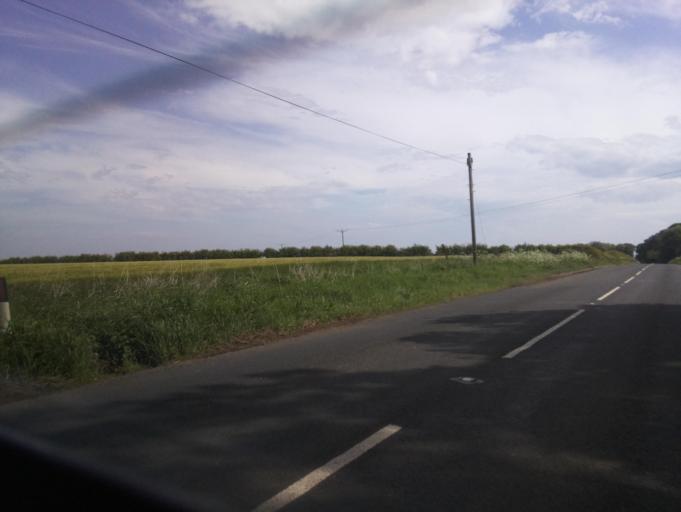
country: GB
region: England
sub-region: Northumberland
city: Alnwick
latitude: 55.4331
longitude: -1.7073
